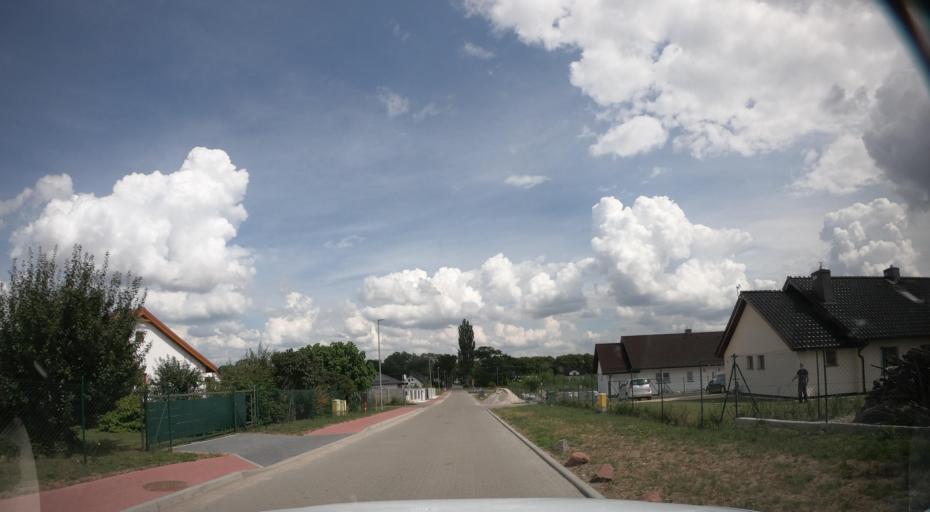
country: PL
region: West Pomeranian Voivodeship
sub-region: Powiat pyrzycki
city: Pyrzyce
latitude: 53.1337
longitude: 14.8844
